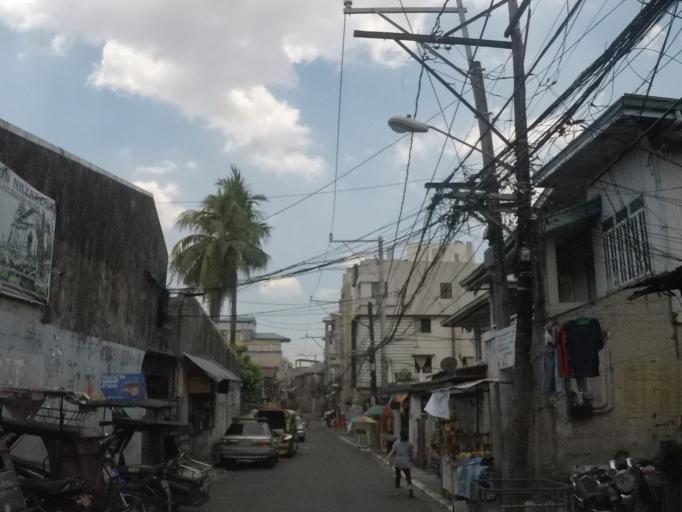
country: PH
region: Metro Manila
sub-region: San Juan
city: San Juan
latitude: 14.6057
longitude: 121.0216
